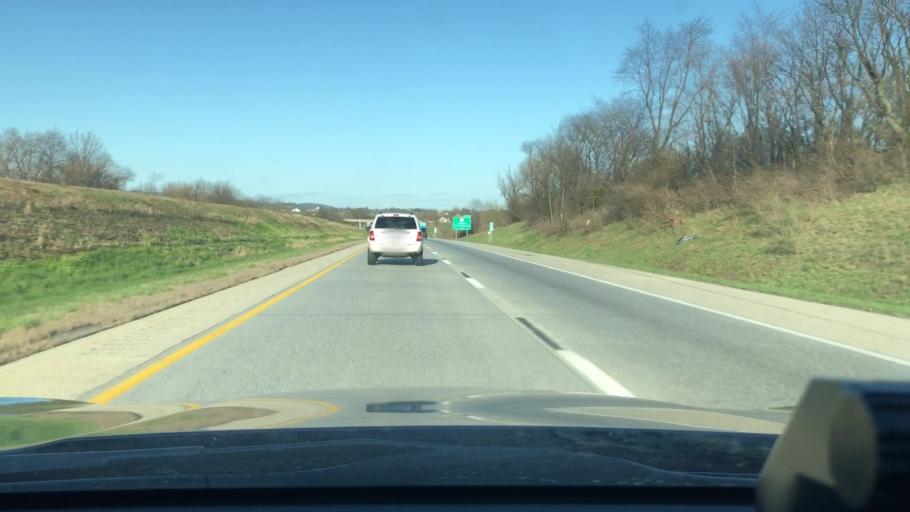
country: US
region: Pennsylvania
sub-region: Lebanon County
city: Fredericksburg
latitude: 40.4505
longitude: -76.4421
